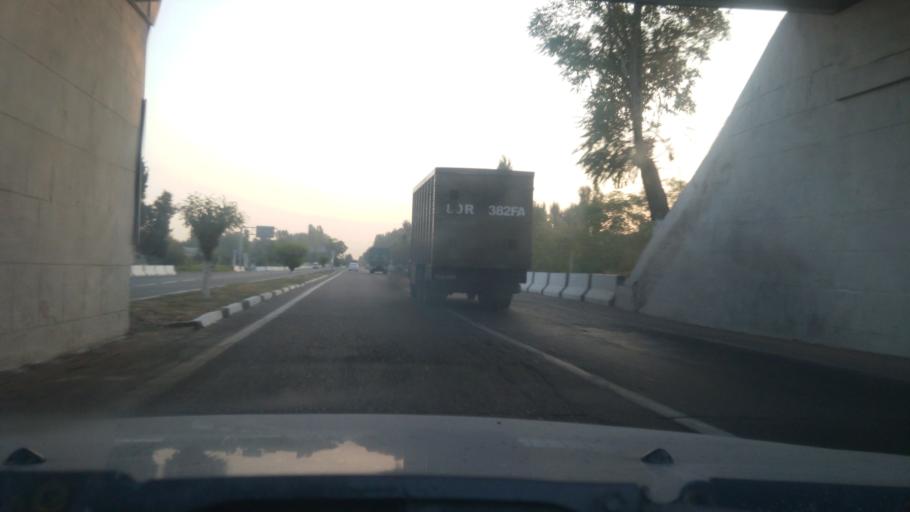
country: UZ
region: Toshkent
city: Yangiyul
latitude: 41.1057
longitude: 68.9740
